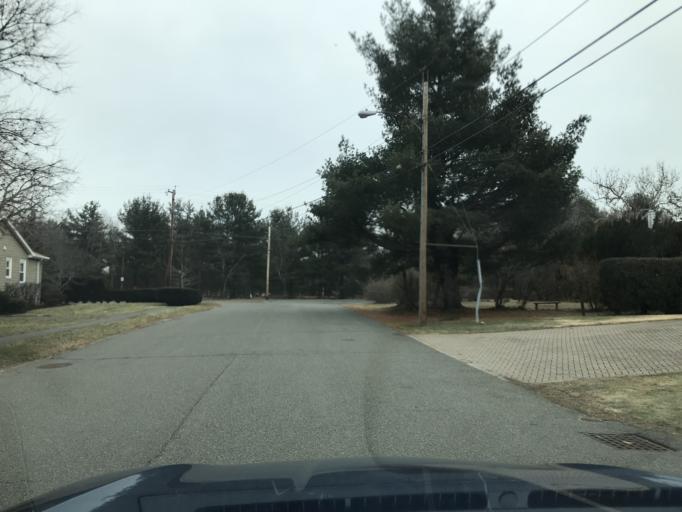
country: US
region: Massachusetts
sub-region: Essex County
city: Saugus
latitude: 42.4802
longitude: -71.0269
